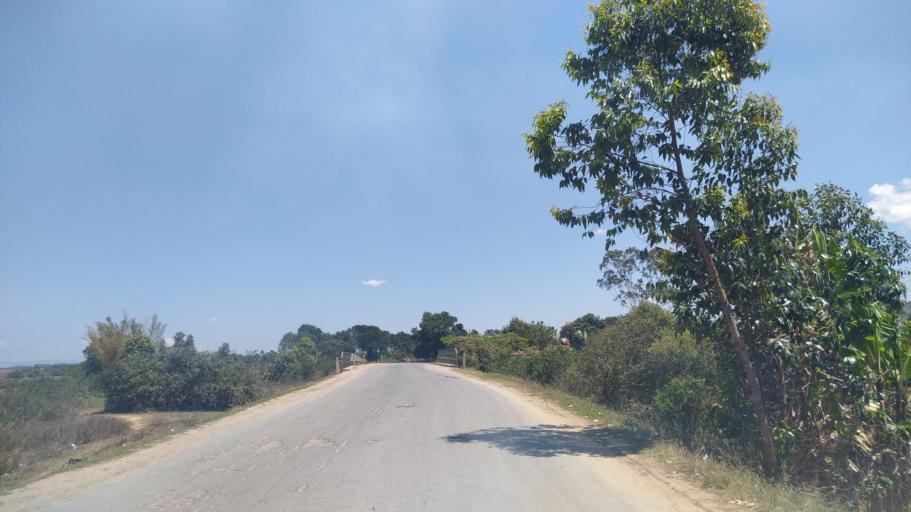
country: MG
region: Alaotra Mangoro
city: Moramanga
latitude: -18.7299
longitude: 48.2656
